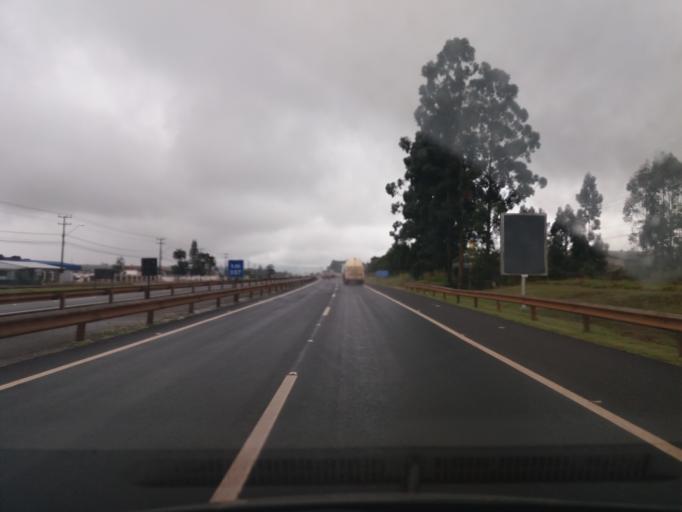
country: BR
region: Parana
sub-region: Cascavel
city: Cascavel
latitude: -24.9954
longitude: -53.5143
